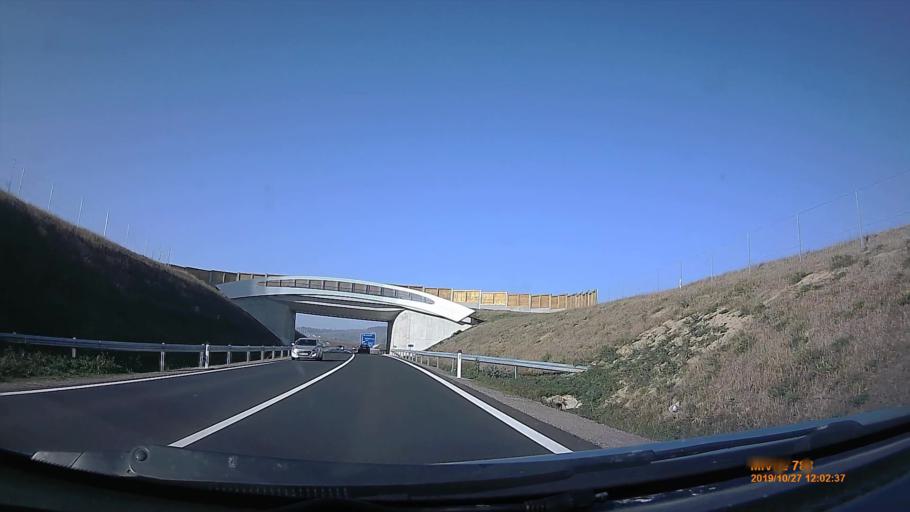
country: AT
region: Lower Austria
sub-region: Politischer Bezirk Mistelbach
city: Drasenhofen
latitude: 48.7362
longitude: 16.6489
